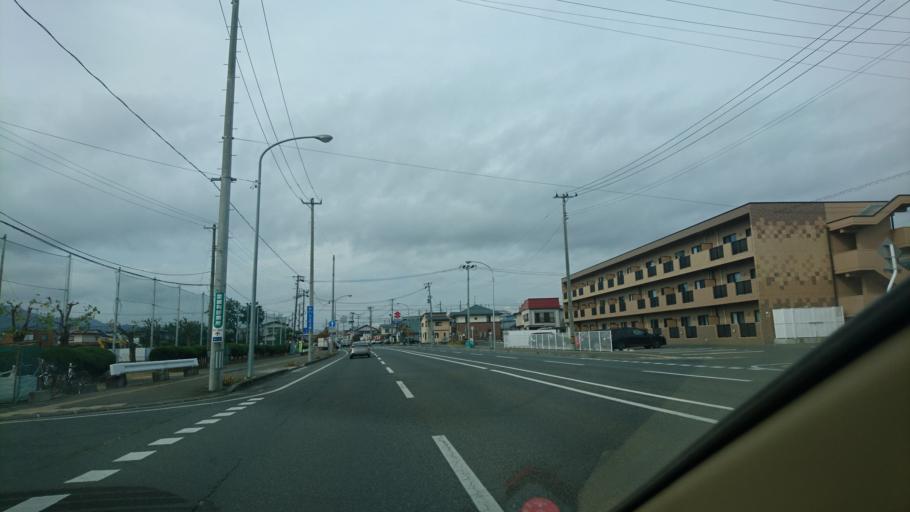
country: JP
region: Iwate
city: Morioka-shi
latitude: 39.6846
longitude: 141.1544
